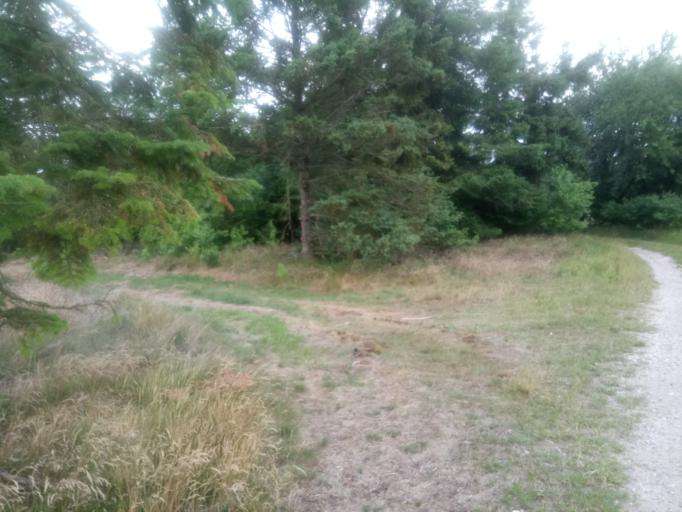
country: DK
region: Central Jutland
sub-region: Ringkobing-Skjern Kommune
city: Tarm
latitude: 55.9425
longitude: 8.6518
